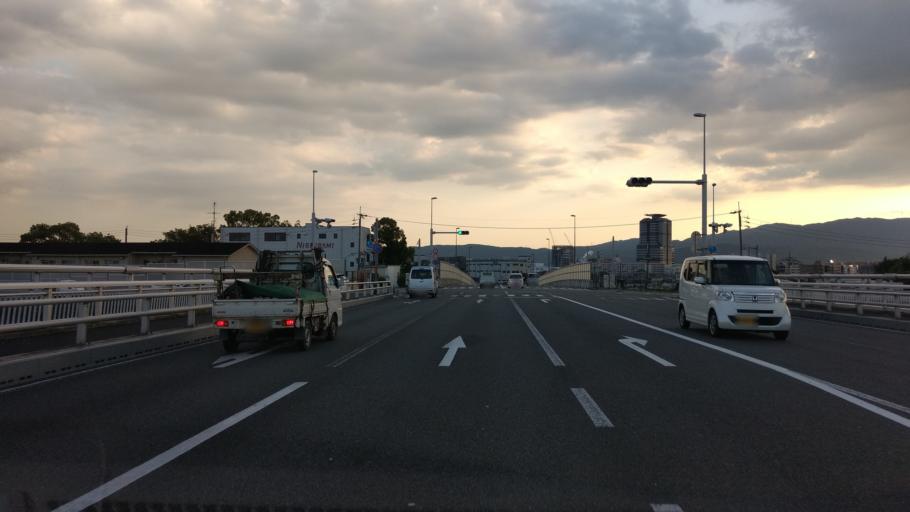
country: JP
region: Kyoto
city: Muko
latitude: 34.9569
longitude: 135.7272
